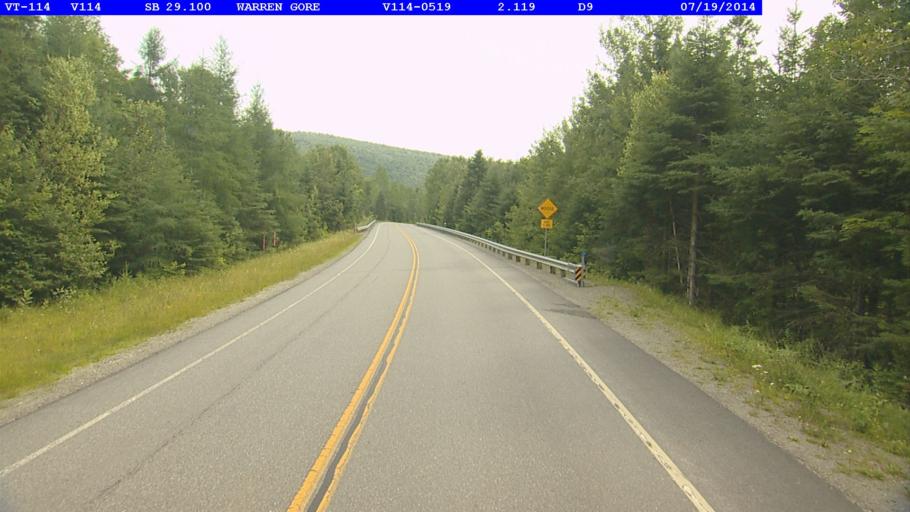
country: CA
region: Quebec
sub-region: Estrie
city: Coaticook
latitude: 44.9143
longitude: -71.8755
